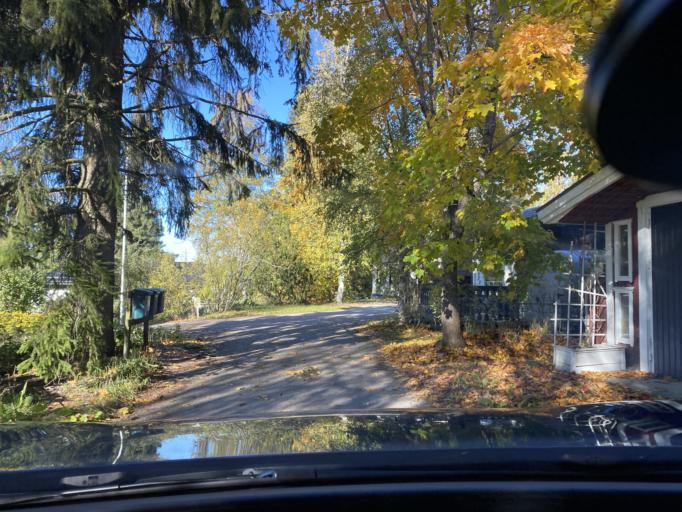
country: FI
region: Satakunta
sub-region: Rauma
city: Eura
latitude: 61.1335
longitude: 22.1399
